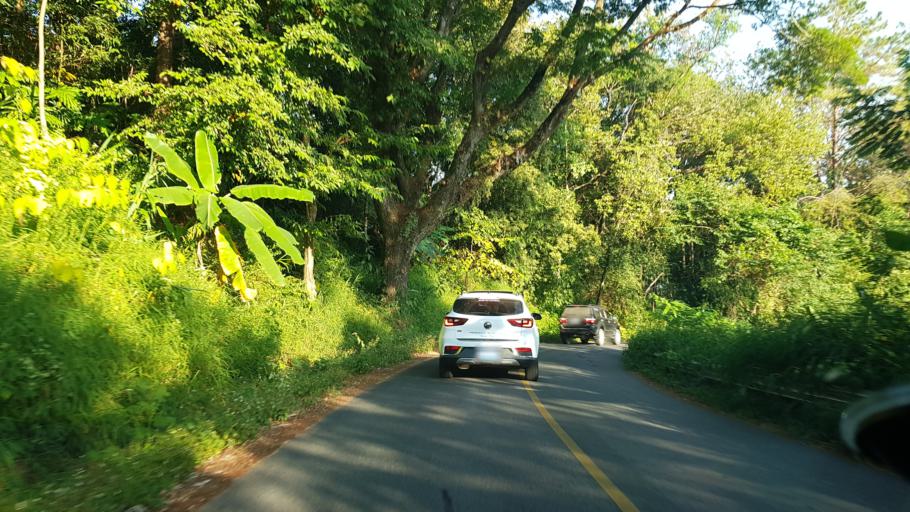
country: TH
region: Chiang Rai
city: Mae Fa Luang
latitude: 20.3132
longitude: 99.8193
